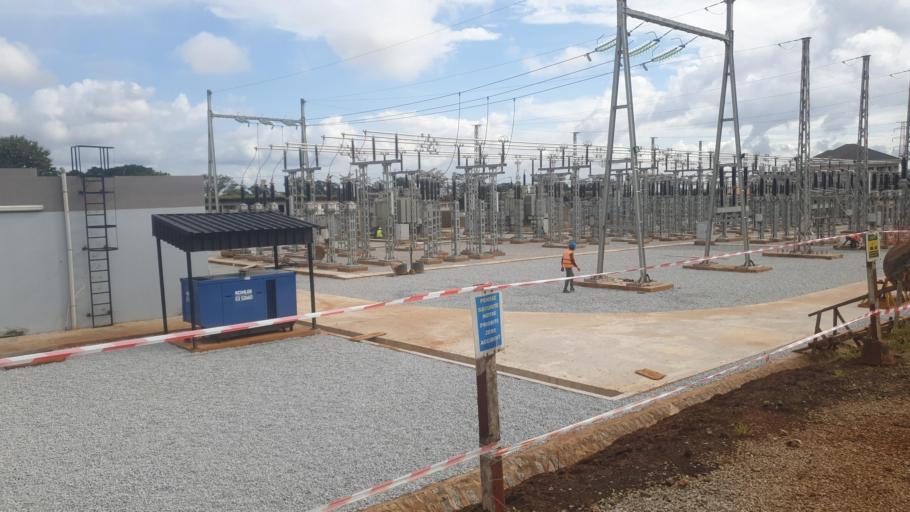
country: GN
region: Kindia
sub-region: Prefecture de Dubreka
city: Dubreka
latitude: 9.7201
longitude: -13.4897
